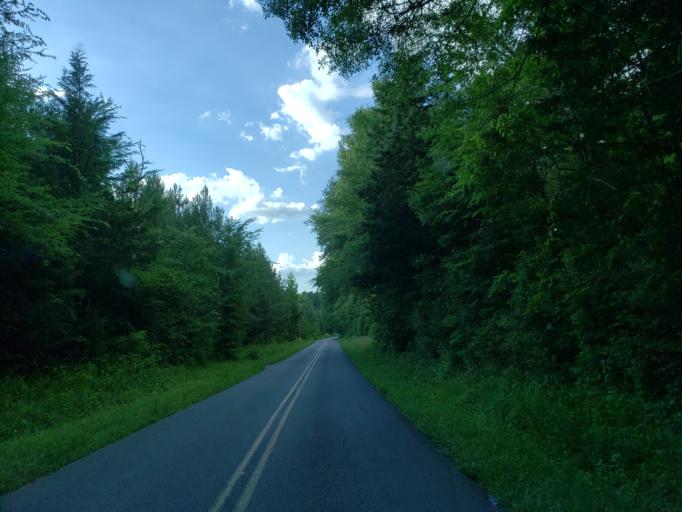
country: US
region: Georgia
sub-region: Polk County
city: Cedartown
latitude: 33.9295
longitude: -85.2711
